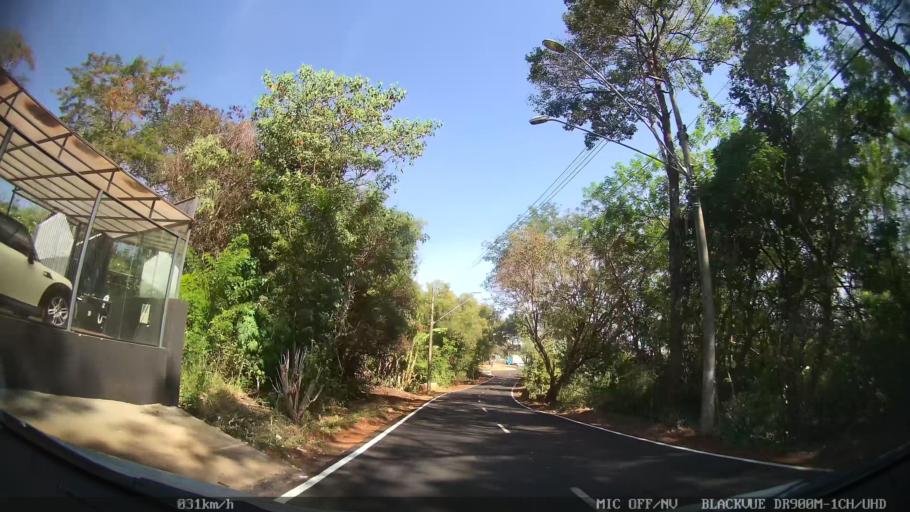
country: BR
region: Sao Paulo
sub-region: Ribeirao Preto
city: Ribeirao Preto
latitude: -21.2048
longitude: -47.8278
